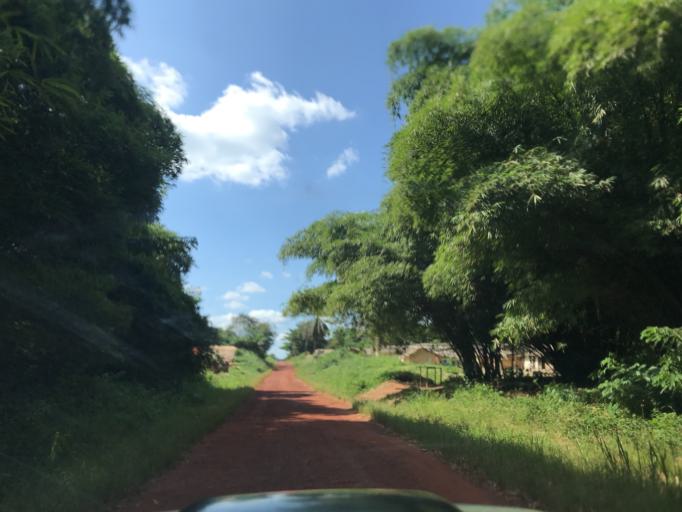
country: CD
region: Eastern Province
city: Kisangani
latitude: 1.2409
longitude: 25.2720
